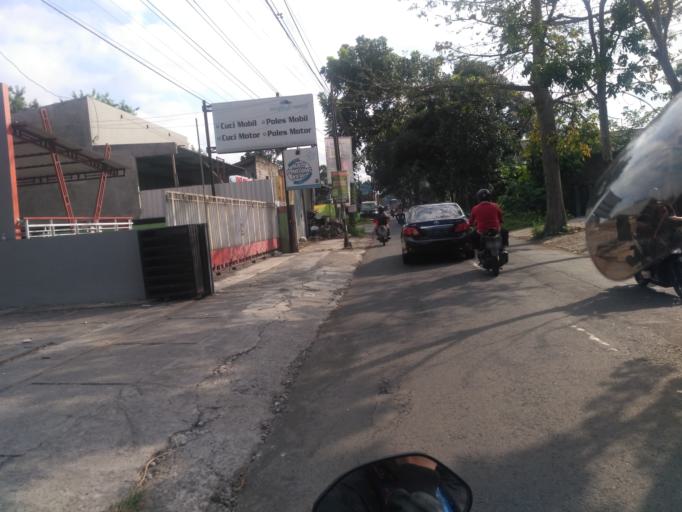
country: ID
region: Daerah Istimewa Yogyakarta
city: Yogyakarta
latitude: -7.7568
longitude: 110.3465
